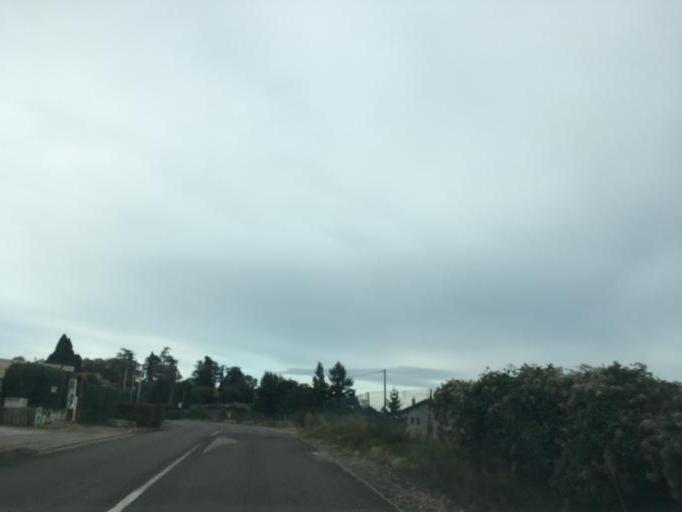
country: FR
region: Rhone-Alpes
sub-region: Departement de la Loire
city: Saint-Martin-la-Plaine
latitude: 45.5406
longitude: 4.5934
